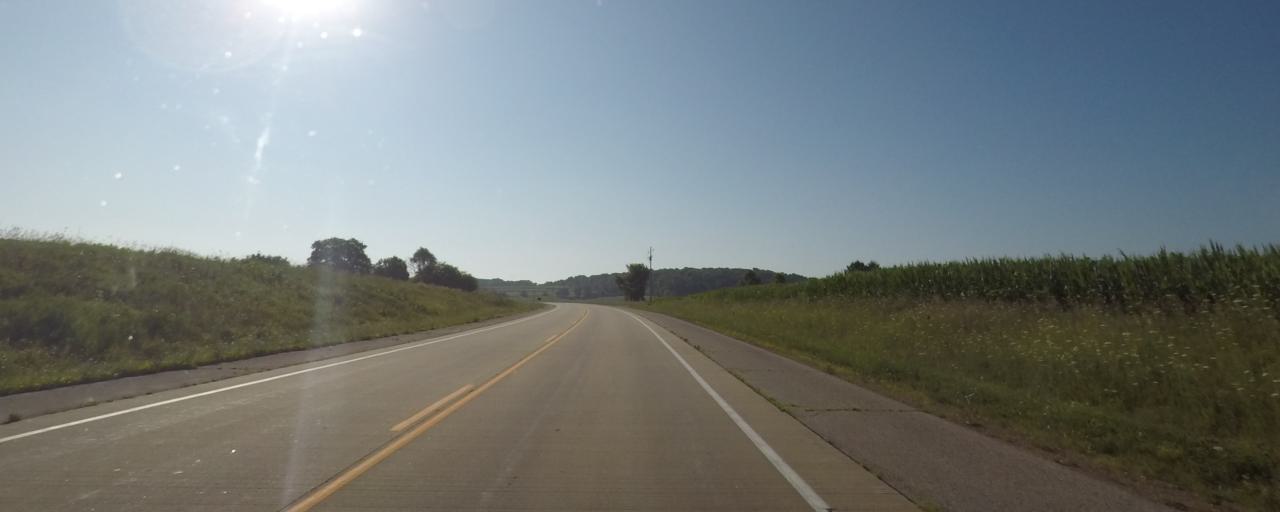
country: US
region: Wisconsin
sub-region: Jefferson County
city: Lake Ripley
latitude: 42.9748
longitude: -88.9492
